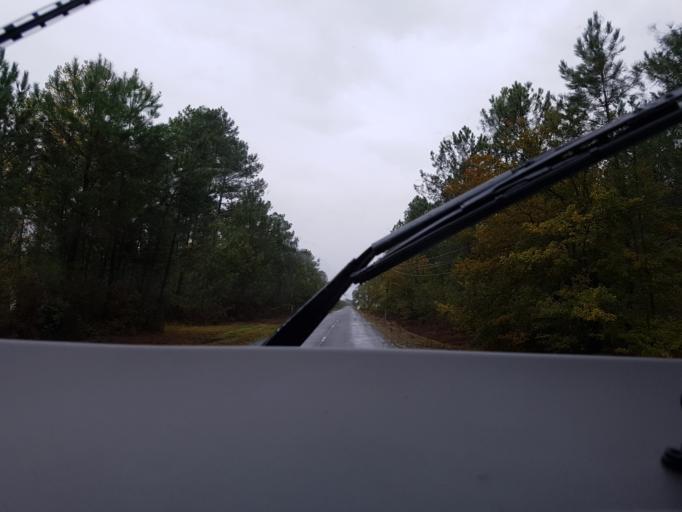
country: FR
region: Aquitaine
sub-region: Departement de la Gironde
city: Saint-Symphorien
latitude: 44.3501
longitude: -0.6193
